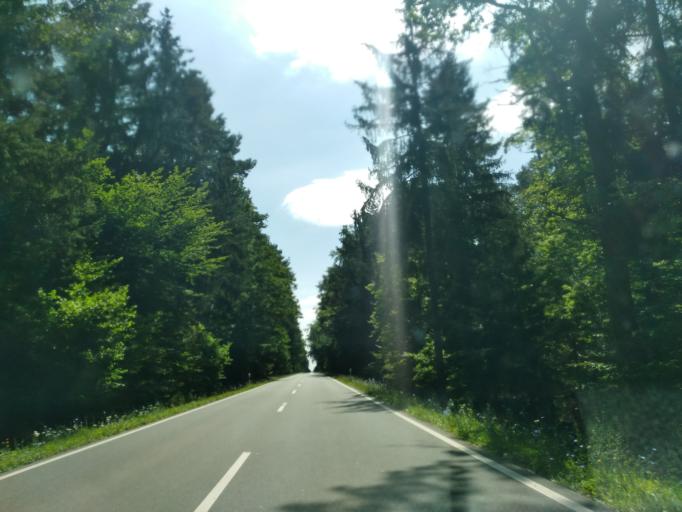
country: DE
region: Baden-Wuerttemberg
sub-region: Karlsruhe Region
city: Mudau
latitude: 49.5082
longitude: 9.2281
